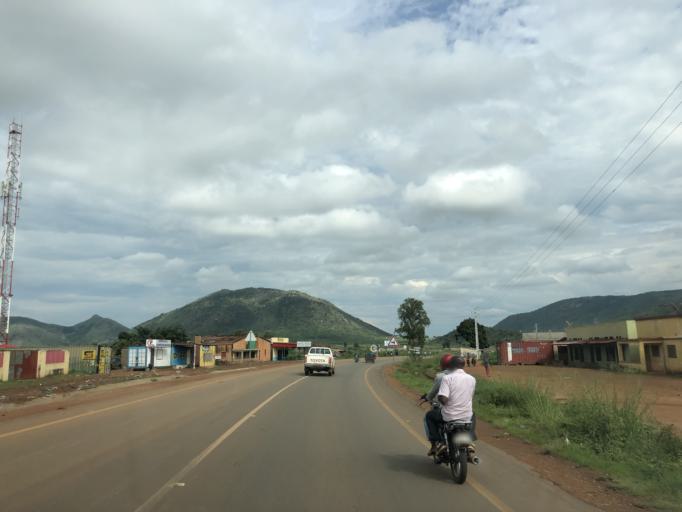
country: AO
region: Cuanza Sul
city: Uacu Cungo
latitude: -11.3490
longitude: 15.1055
